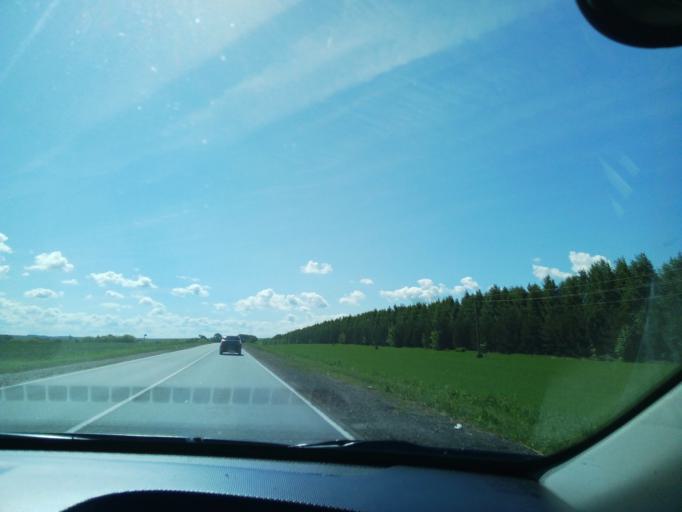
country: RU
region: Chuvashia
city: Atlashevo
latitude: 56.0476
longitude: 47.5217
